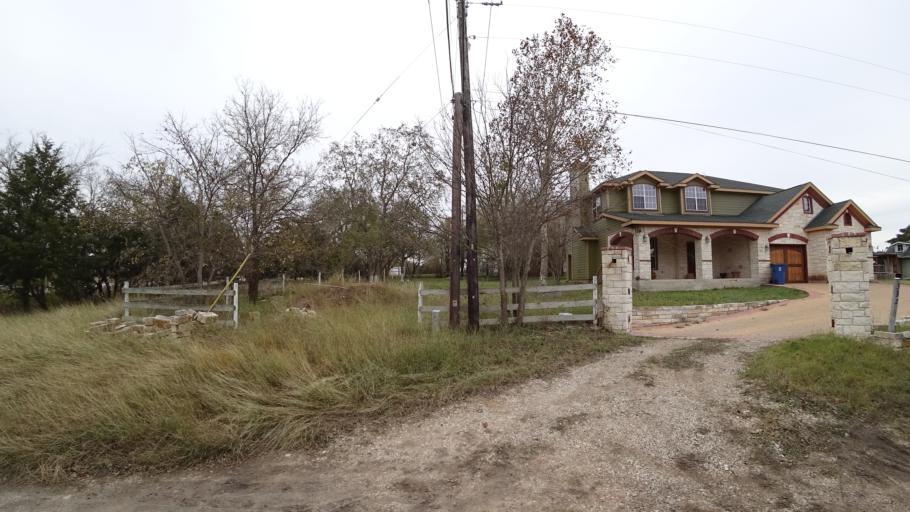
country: US
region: Texas
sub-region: Travis County
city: Garfield
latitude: 30.1084
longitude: -97.5876
